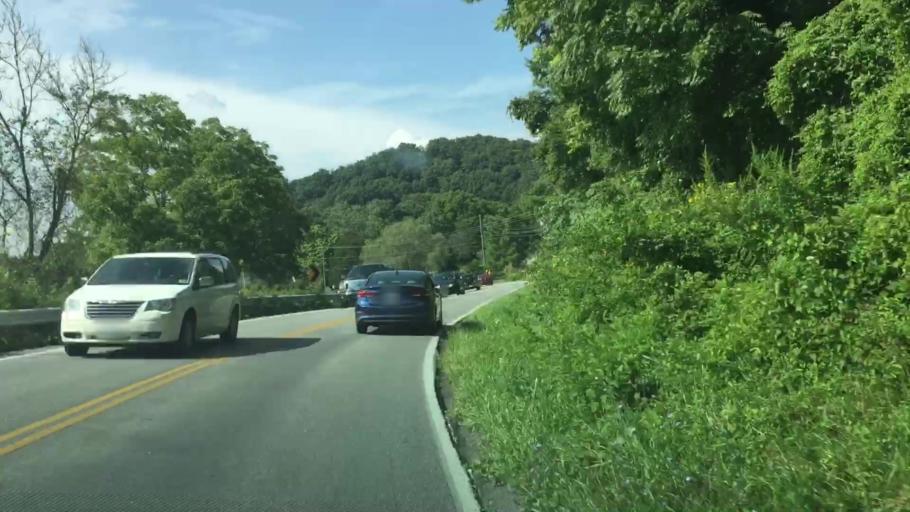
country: US
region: Tennessee
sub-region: Sullivan County
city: Fairmount
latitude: 36.6029
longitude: -82.1268
